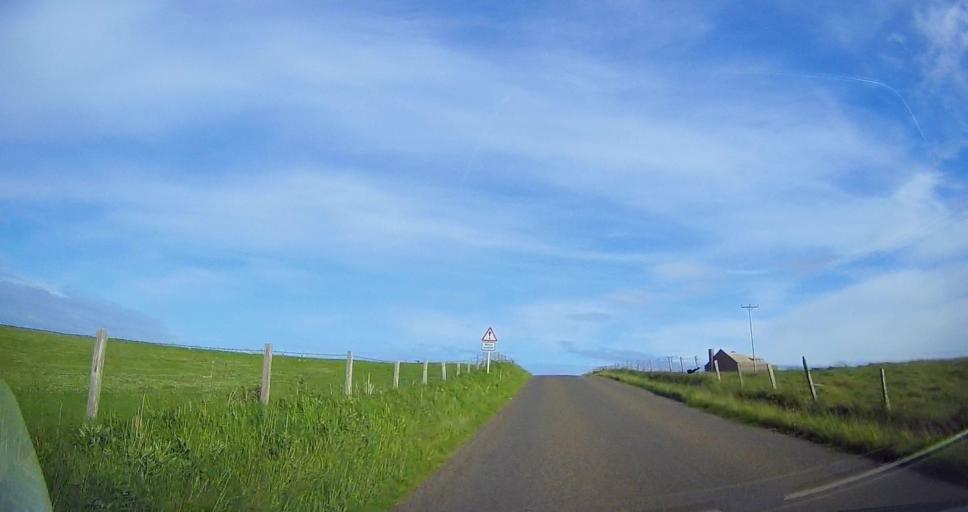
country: GB
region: Scotland
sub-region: Orkney Islands
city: Stromness
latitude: 58.8239
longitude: -3.2102
